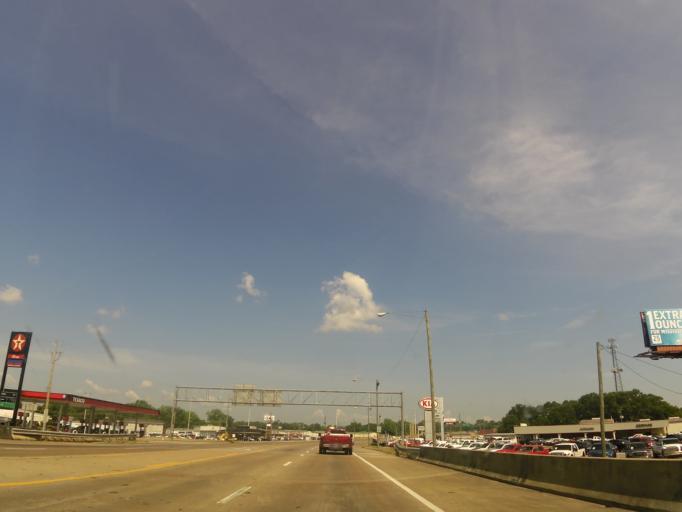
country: US
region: Mississippi
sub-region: Lauderdale County
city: Meridian
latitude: 32.3686
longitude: -88.6765
